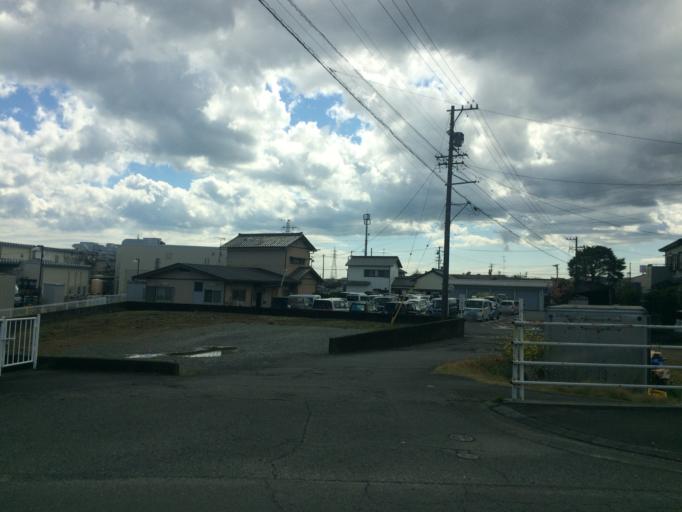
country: JP
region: Shizuoka
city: Fujieda
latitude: 34.7915
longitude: 138.2554
